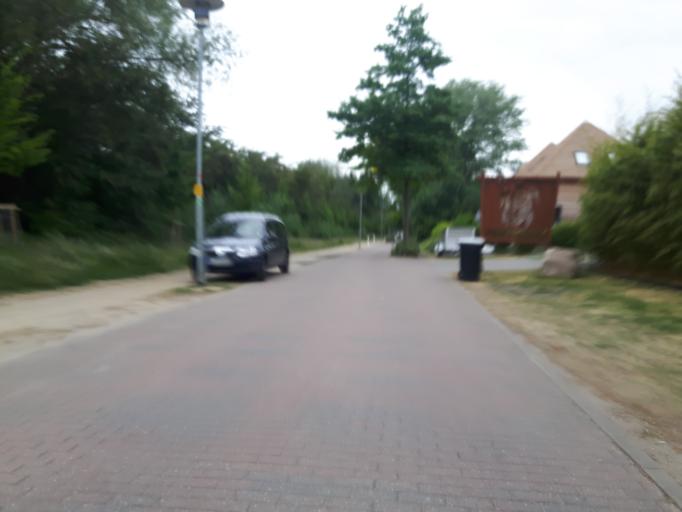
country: DE
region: Schleswig-Holstein
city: Schashagen
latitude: 54.0876
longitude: 10.8700
